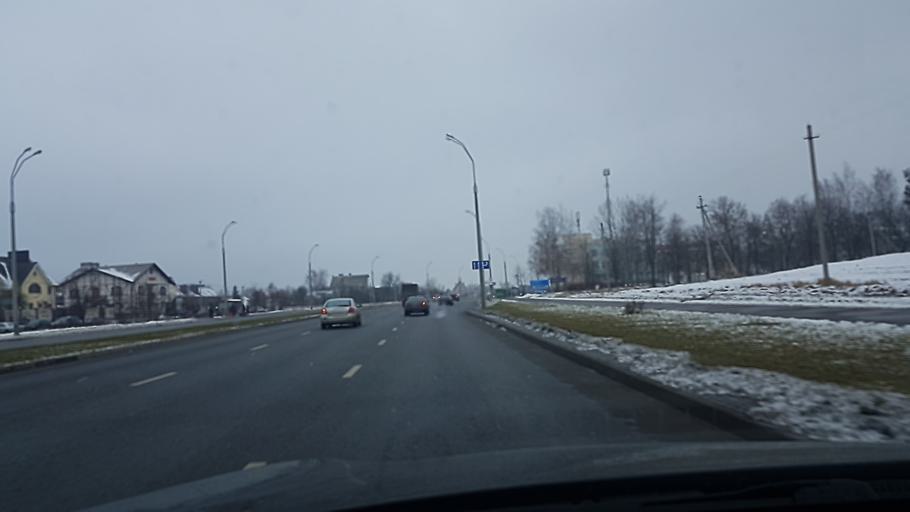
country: BY
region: Minsk
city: Minsk
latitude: 53.9513
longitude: 27.5355
